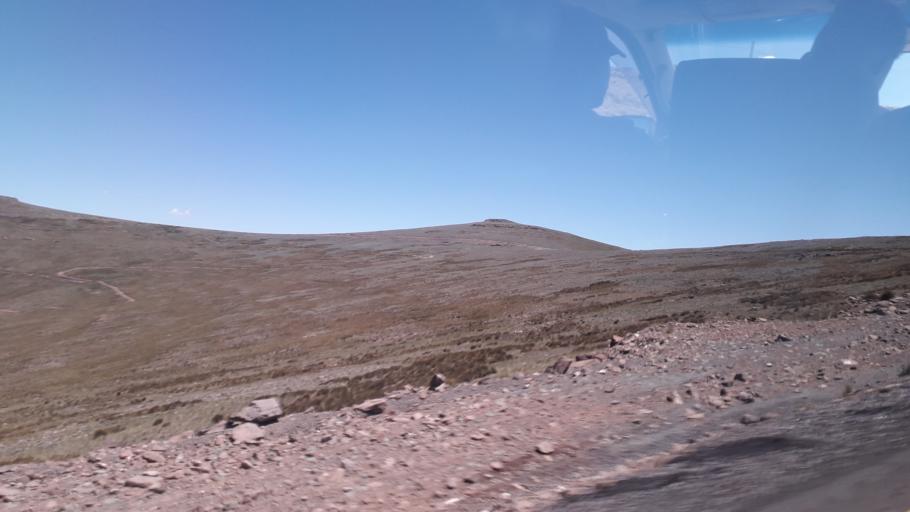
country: ZA
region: Orange Free State
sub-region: Thabo Mofutsanyana District Municipality
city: Phuthaditjhaba
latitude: -28.8181
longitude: 28.7353
